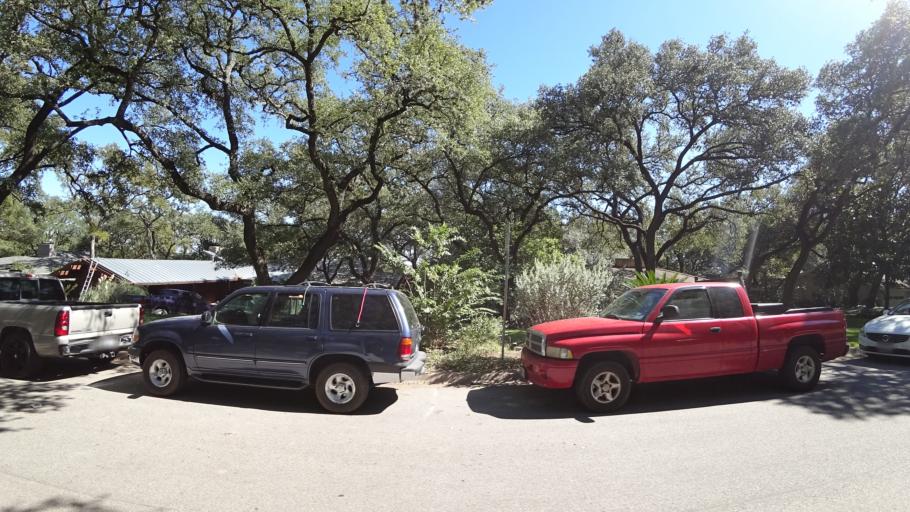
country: US
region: Texas
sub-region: Travis County
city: West Lake Hills
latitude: 30.3221
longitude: -97.7687
